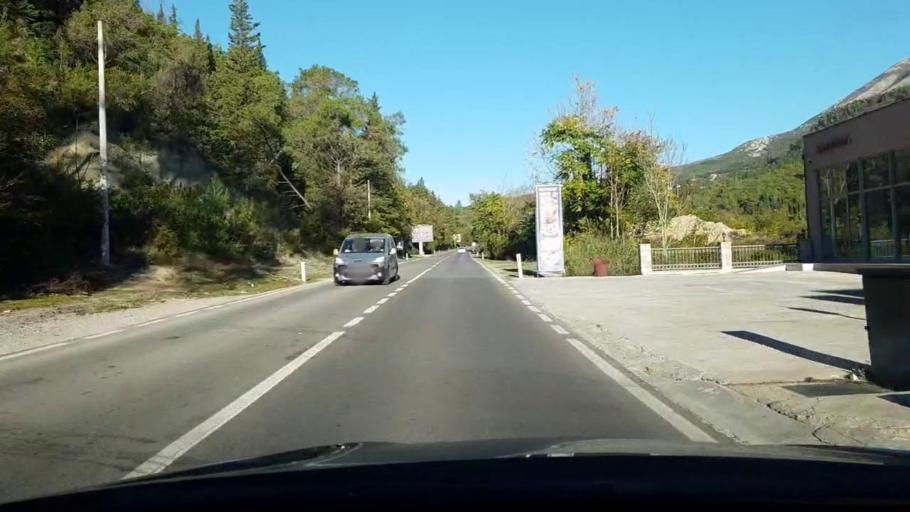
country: ME
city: Igalo
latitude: 42.4765
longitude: 18.4645
